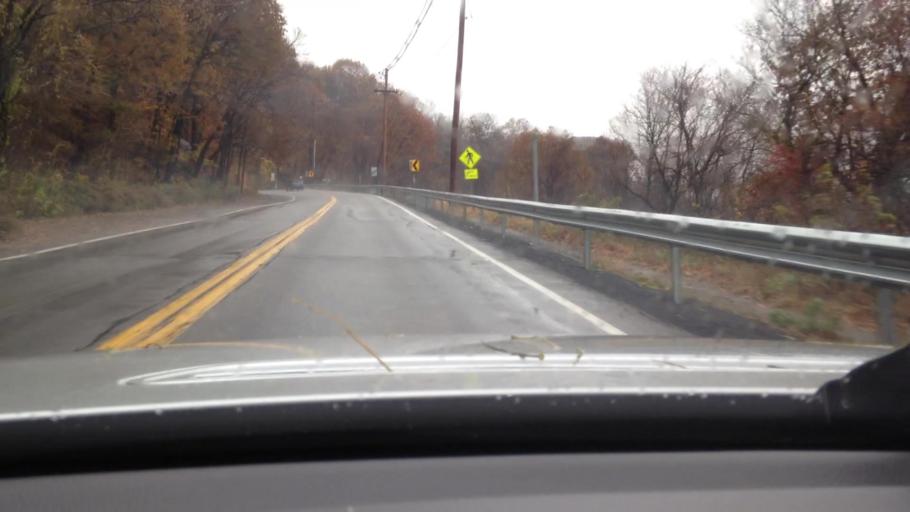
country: US
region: New York
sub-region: Putnam County
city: Cold Spring
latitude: 41.4447
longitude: -73.9788
